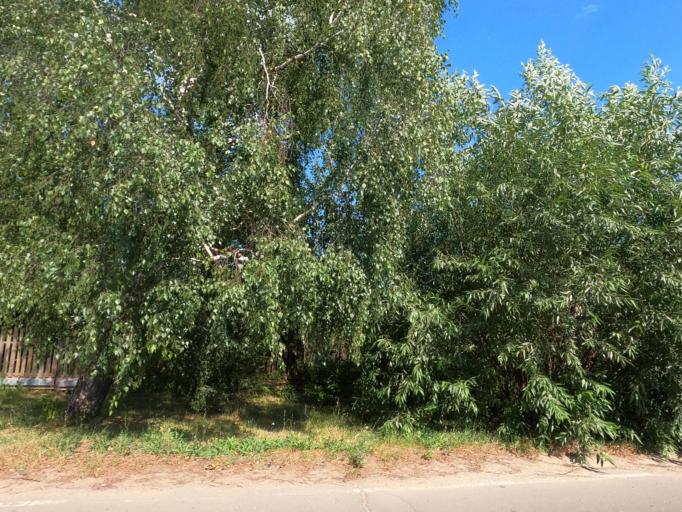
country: RU
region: Moskovskaya
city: Peski
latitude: 55.2267
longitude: 38.7509
